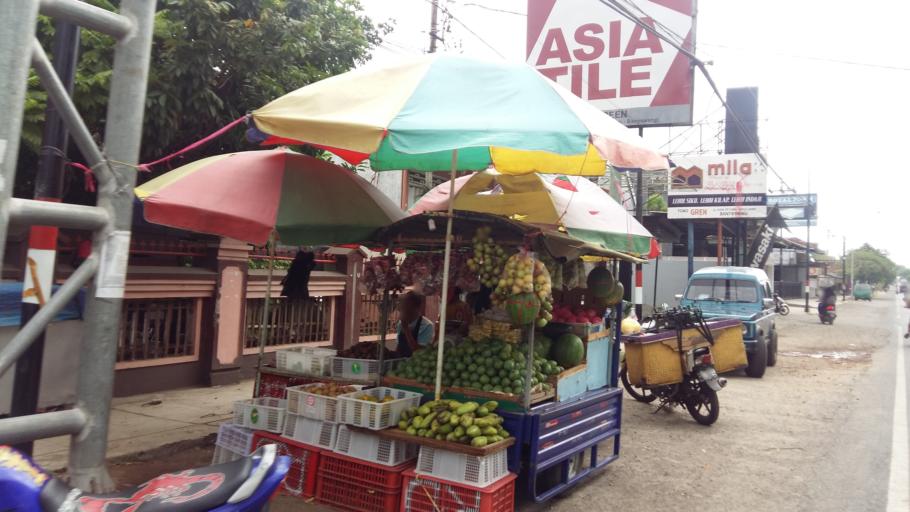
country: ID
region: East Java
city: Krajan
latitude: -8.3144
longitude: 114.2888
